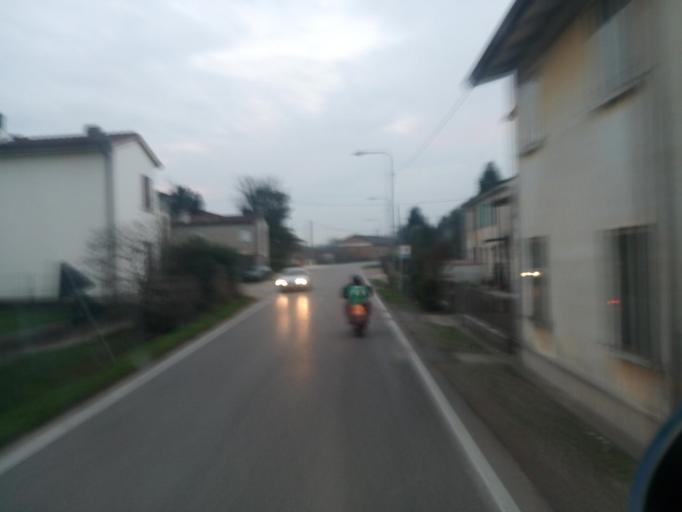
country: IT
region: Lombardy
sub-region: Provincia di Mantova
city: Roncoferraro
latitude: 45.1414
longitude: 10.9372
